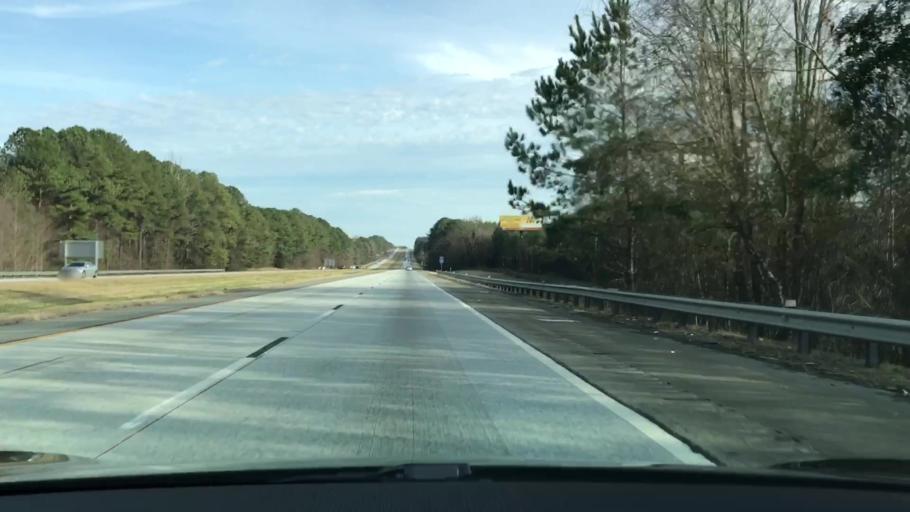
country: US
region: Georgia
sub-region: Putnam County
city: Jefferson
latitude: 33.5487
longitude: -83.3485
